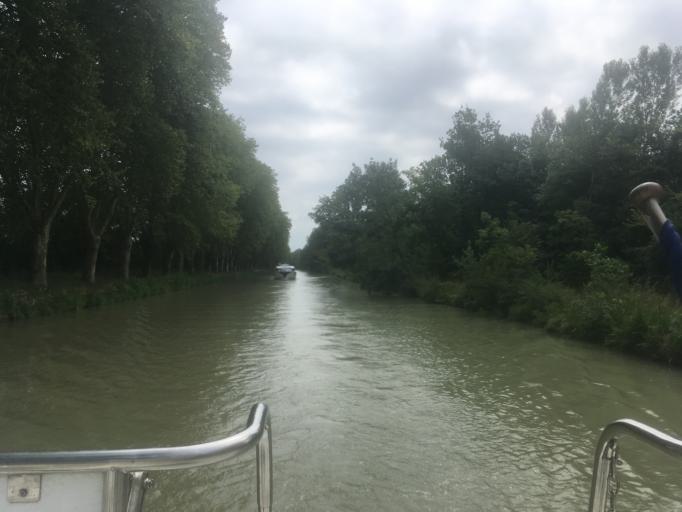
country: FR
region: Languedoc-Roussillon
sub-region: Departement de l'Aude
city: Villepinte
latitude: 43.2757
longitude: 2.0818
